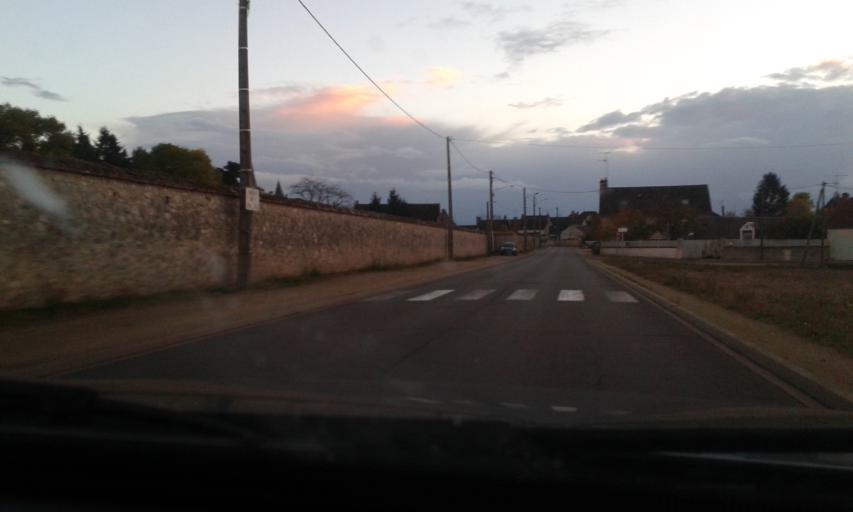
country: FR
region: Centre
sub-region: Departement du Loiret
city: Huisseau-sur-Mauves
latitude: 47.8952
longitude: 1.7044
